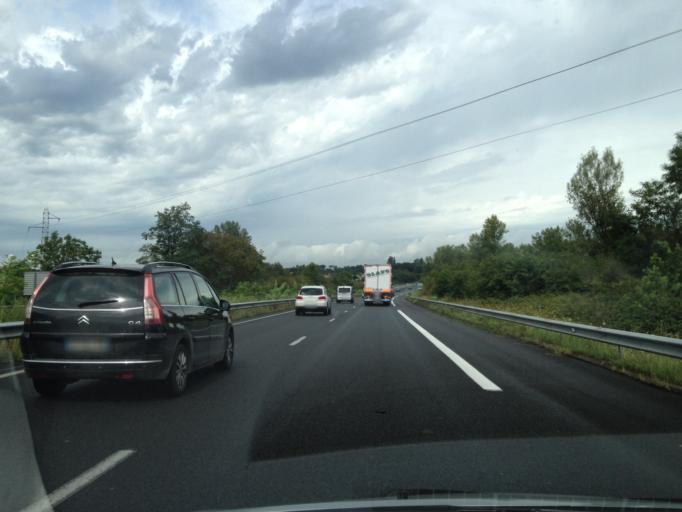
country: FR
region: Aquitaine
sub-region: Departement de la Gironde
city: Langon
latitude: 44.5342
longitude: -0.2509
